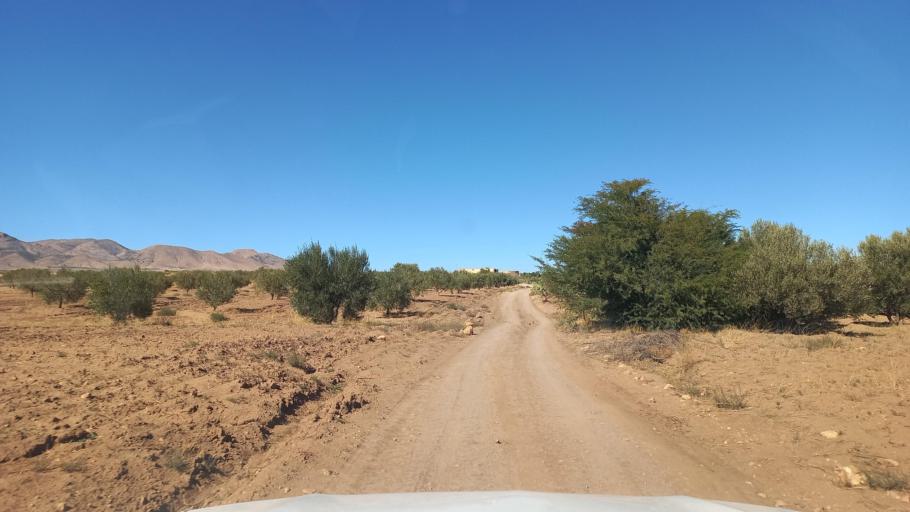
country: TN
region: Al Qasrayn
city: Sbiba
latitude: 35.3959
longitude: 9.0837
